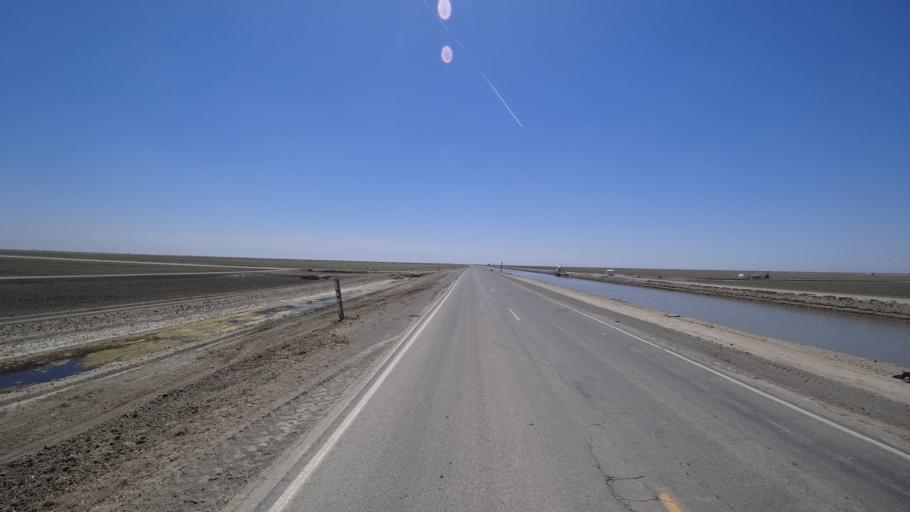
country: US
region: California
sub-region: Kings County
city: Corcoran
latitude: 36.0664
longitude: -119.6438
